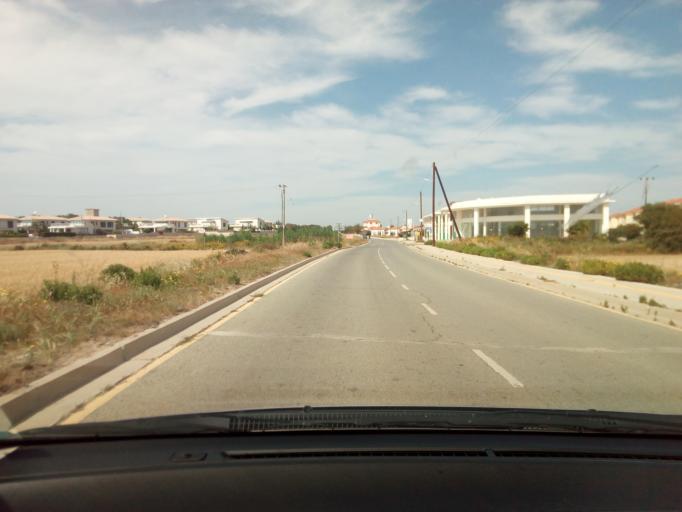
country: CY
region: Larnaka
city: Perivolia
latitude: 34.8289
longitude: 33.6022
